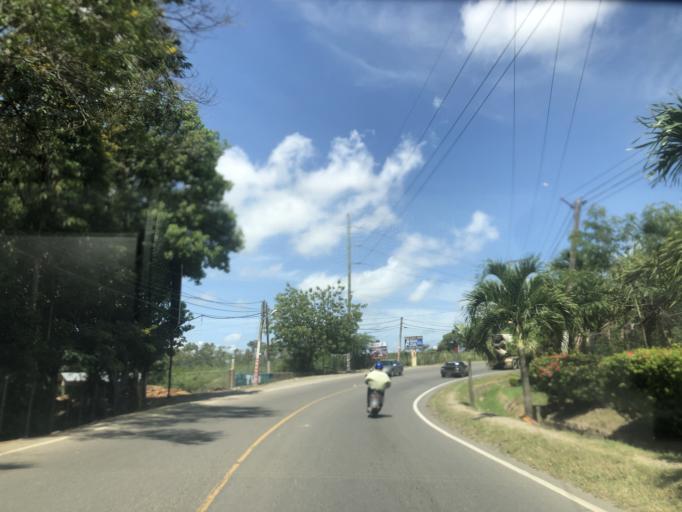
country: DO
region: Santiago
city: La Canela
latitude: 19.4512
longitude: -70.7656
